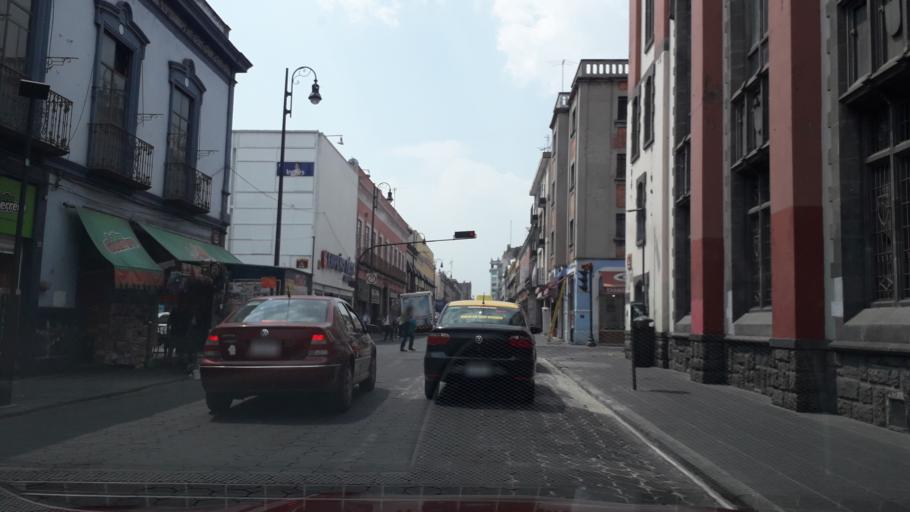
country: MX
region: Puebla
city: Puebla
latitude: 19.0467
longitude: -98.2009
